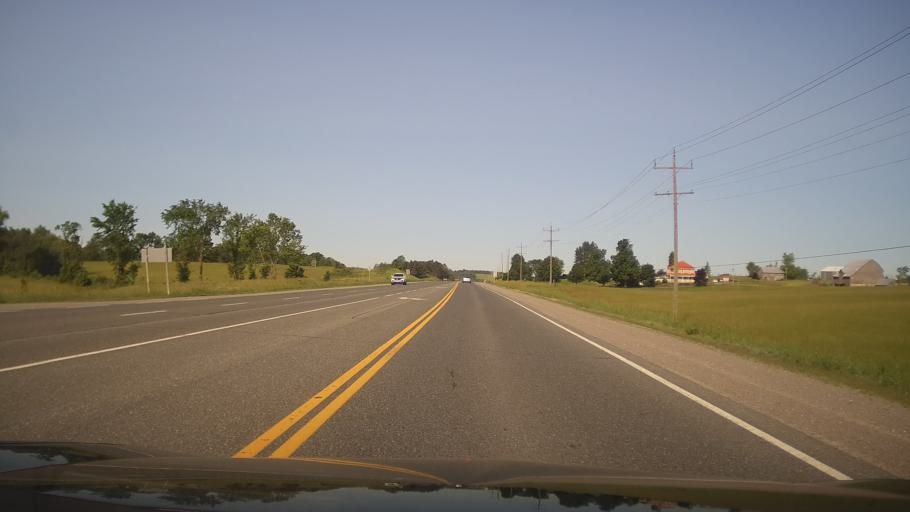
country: CA
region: Ontario
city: Peterborough
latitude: 44.3530
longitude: -78.0554
